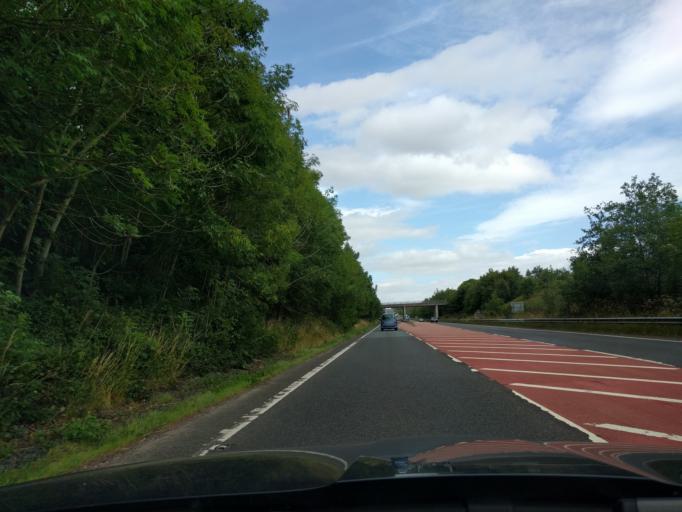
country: GB
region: England
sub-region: Northumberland
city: Felton
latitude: 55.2991
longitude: -1.7264
